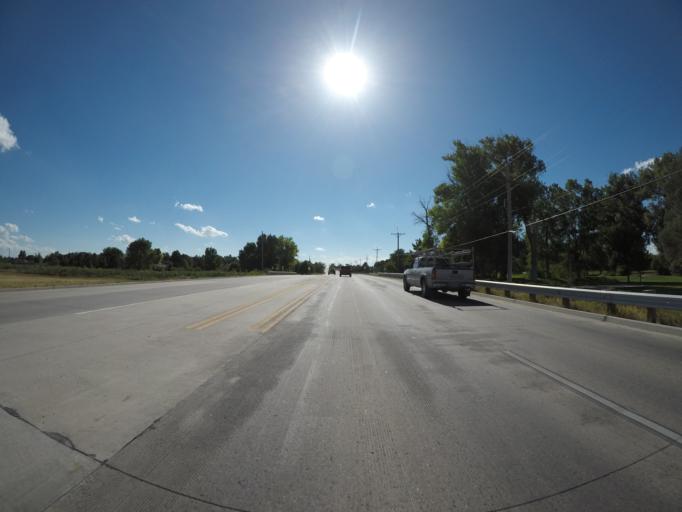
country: US
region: Colorado
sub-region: Logan County
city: Sterling
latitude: 40.6249
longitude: -103.2434
